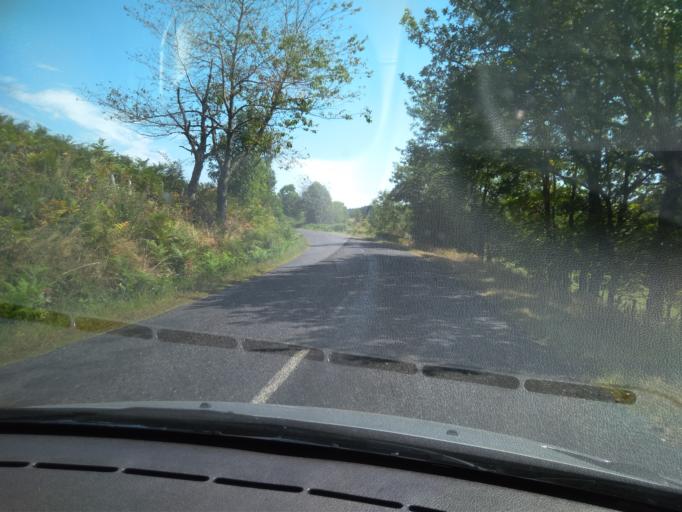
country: FR
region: Rhone-Alpes
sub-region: Departement de la Loire
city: La Pacaudiere
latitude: 46.1338
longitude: 3.7750
